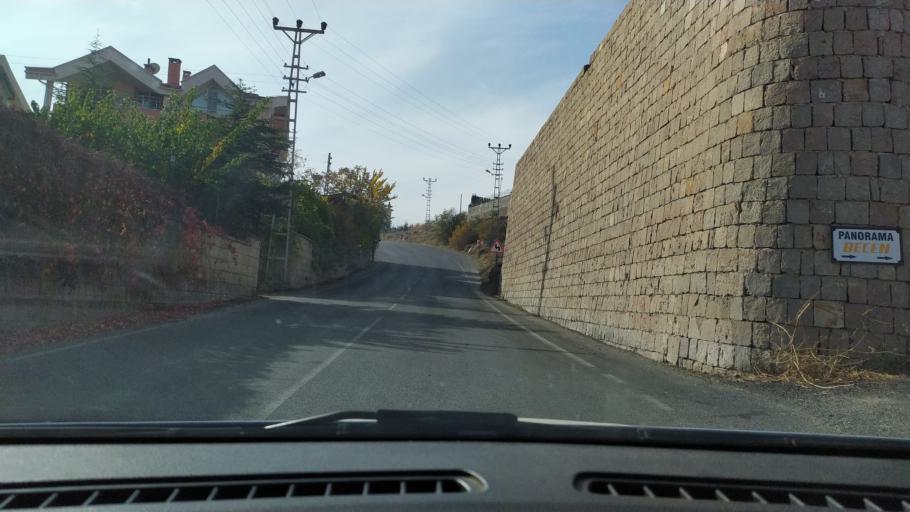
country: TR
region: Kayseri
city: Kayseri
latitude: 38.6808
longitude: 35.4921
